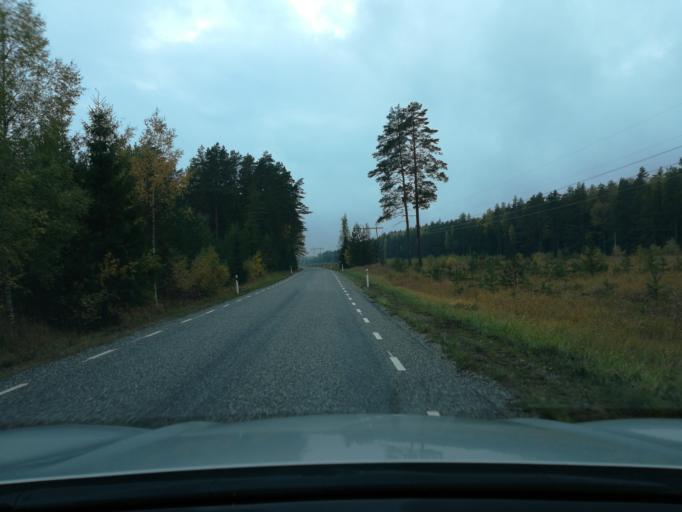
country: EE
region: Ida-Virumaa
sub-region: Johvi vald
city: Johvi
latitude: 59.1643
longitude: 27.4285
